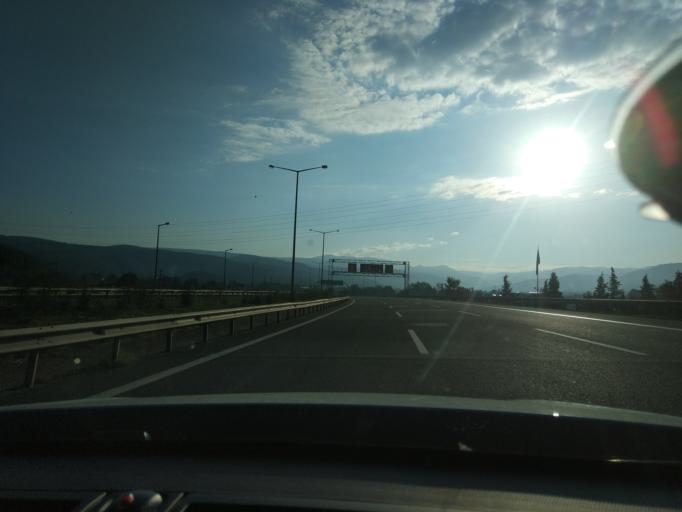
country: TR
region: Duzce
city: Kaynasli
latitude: 40.7853
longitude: 31.2674
